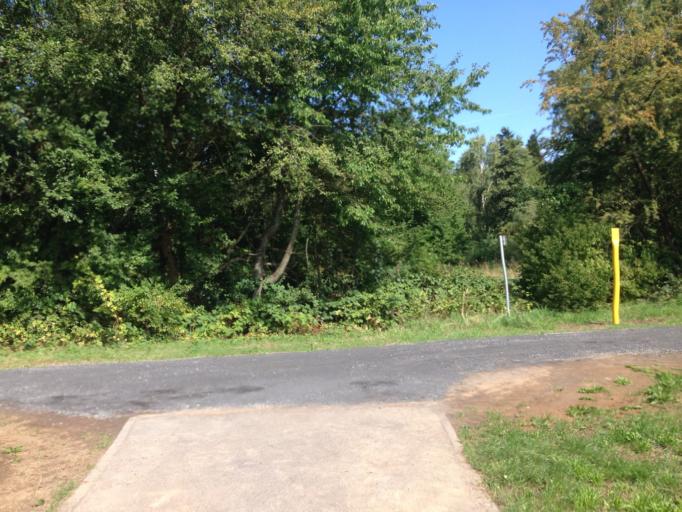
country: DE
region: Hesse
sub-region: Regierungsbezirk Giessen
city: Grunberg
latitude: 50.5864
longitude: 8.9585
